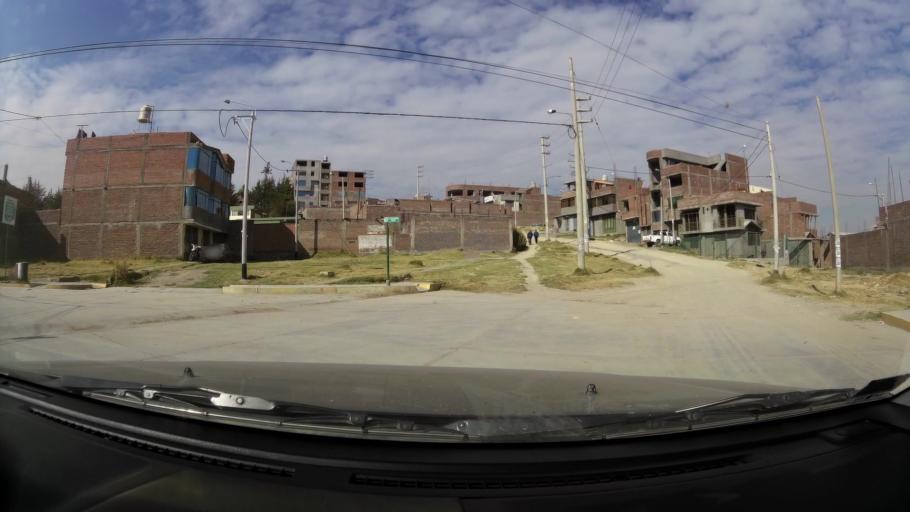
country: PE
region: Junin
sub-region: Provincia de Huancayo
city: Huancayo
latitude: -12.0563
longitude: -75.1934
